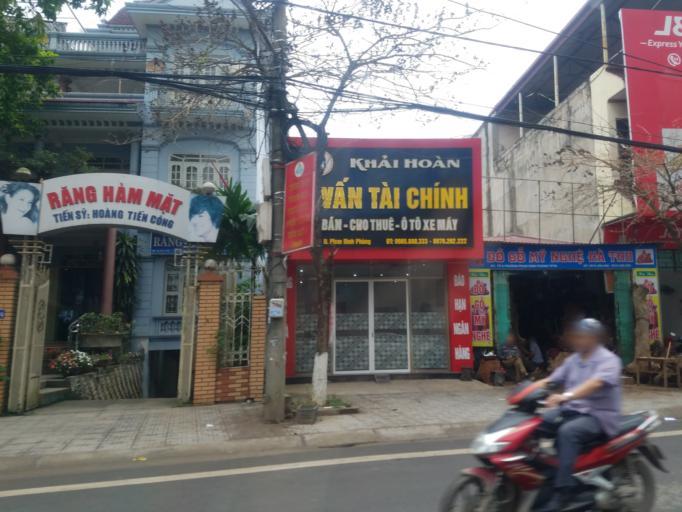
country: VN
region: Thai Nguyen
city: Thanh Pho Thai Nguyen
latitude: 21.5886
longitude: 105.8430
